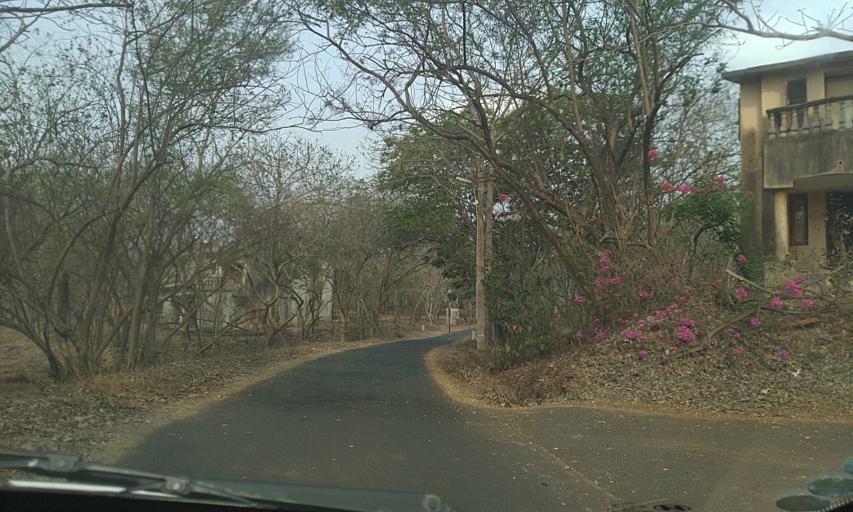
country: IN
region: Goa
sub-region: North Goa
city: Taleigao
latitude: 15.4552
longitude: 73.8364
